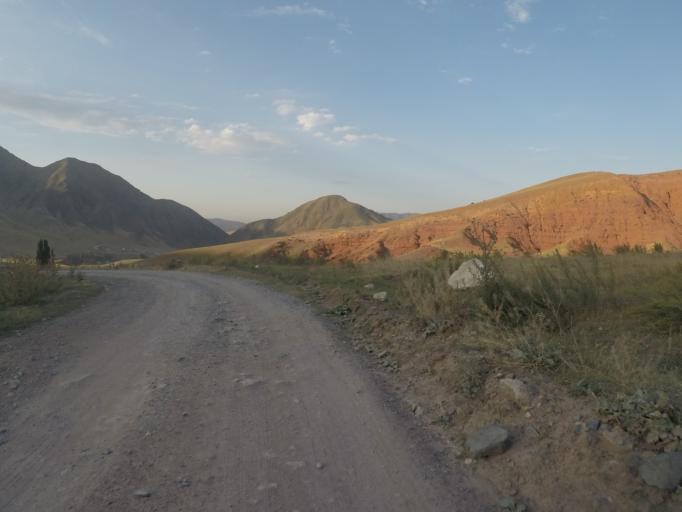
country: KG
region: Chuy
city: Bishkek
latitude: 42.6619
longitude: 74.6510
